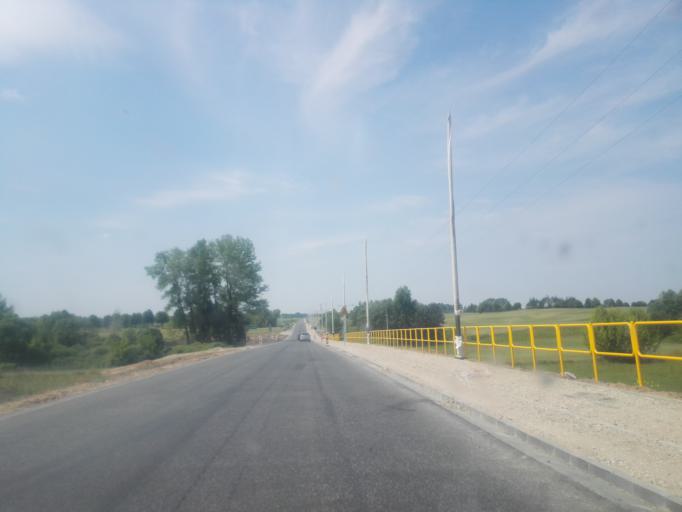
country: PL
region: Podlasie
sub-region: Powiat sejnenski
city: Krasnopol
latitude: 54.0981
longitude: 23.1837
